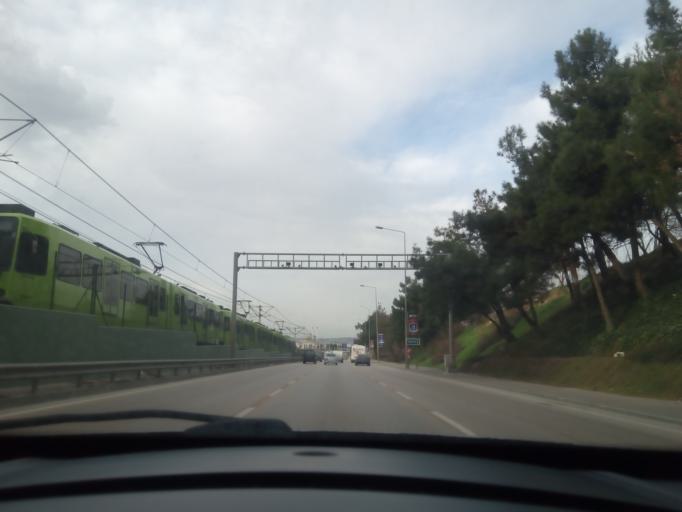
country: TR
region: Bursa
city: Cali
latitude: 40.2124
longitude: 28.9481
